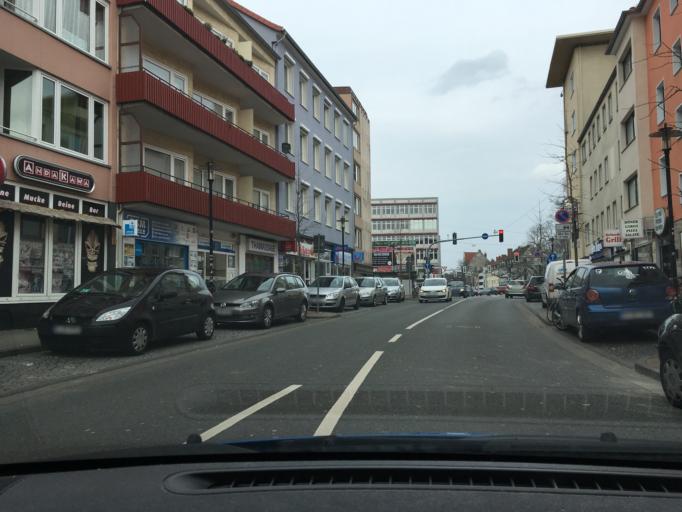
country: DE
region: Lower Saxony
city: Hildesheim
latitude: 52.1493
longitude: 9.9533
